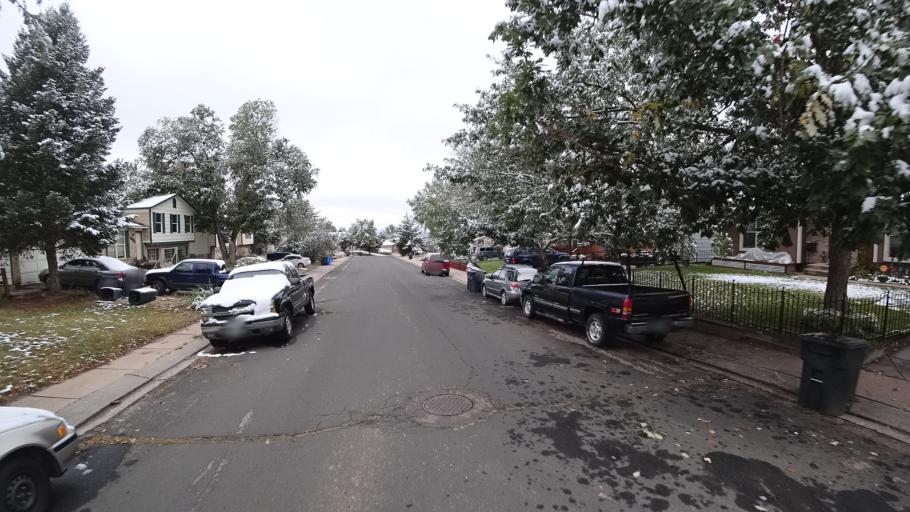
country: US
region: Colorado
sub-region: El Paso County
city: Cimarron Hills
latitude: 38.9281
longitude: -104.7727
